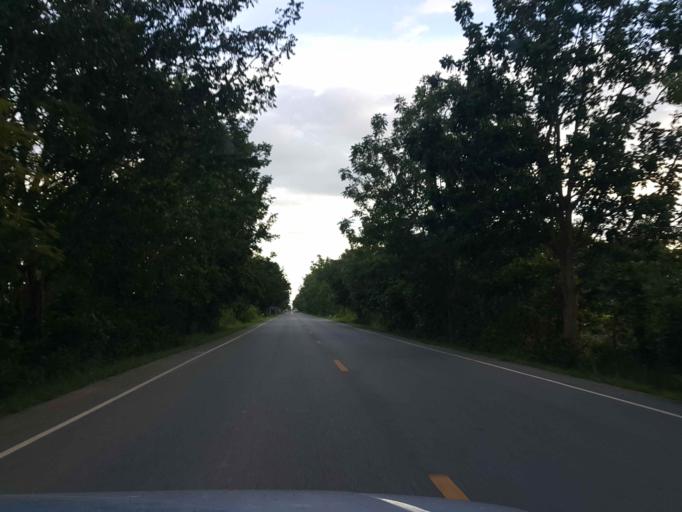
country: TH
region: Sukhothai
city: Sawankhalok
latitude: 17.3163
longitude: 99.7350
